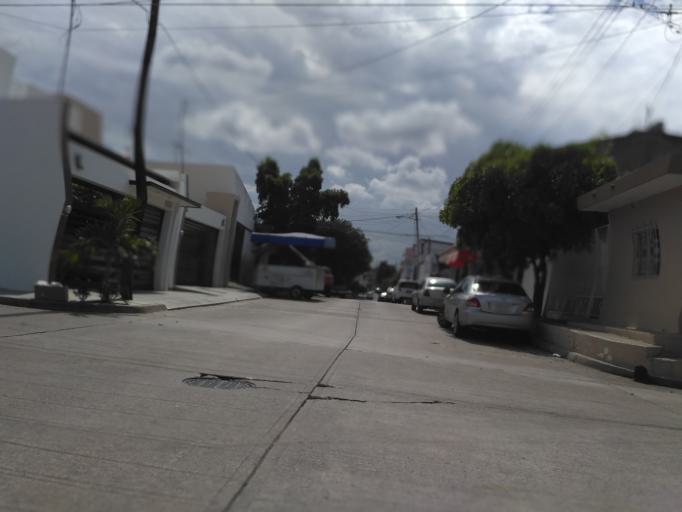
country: MX
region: Sinaloa
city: Culiacan
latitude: 24.7939
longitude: -107.4025
